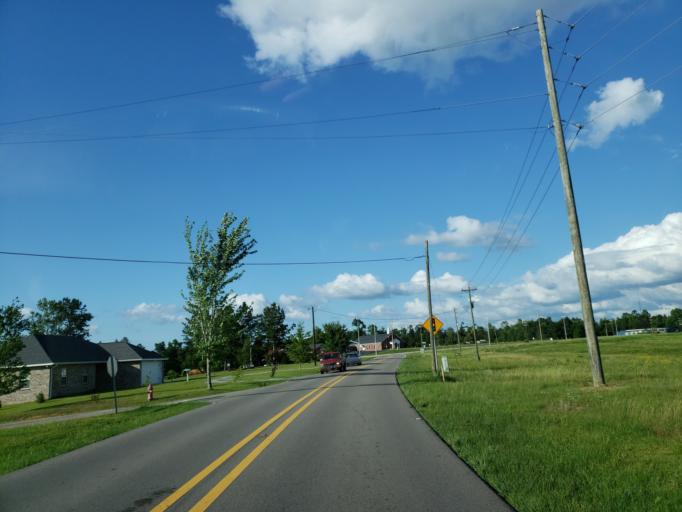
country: US
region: Mississippi
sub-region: Forrest County
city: Petal
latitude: 31.3485
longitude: -89.2305
